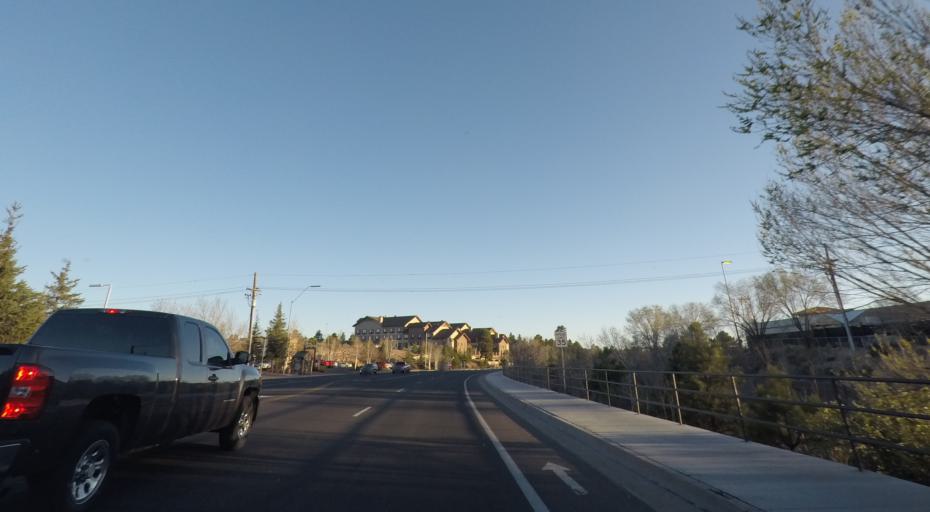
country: US
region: Arizona
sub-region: Coconino County
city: Flagstaff
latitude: 35.1771
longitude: -111.6631
